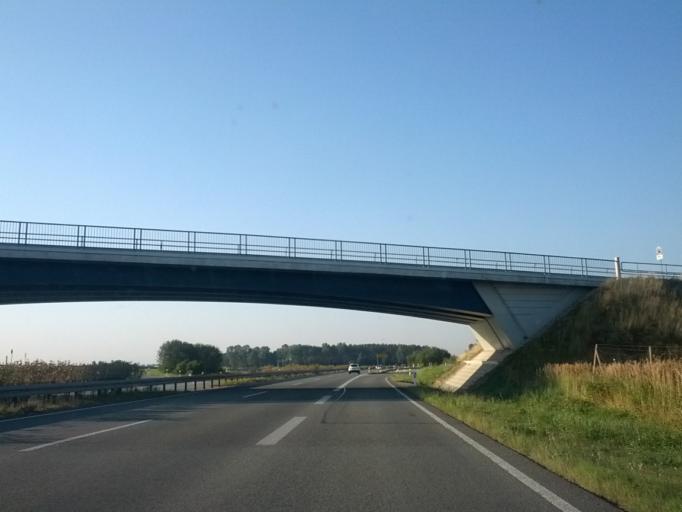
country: DE
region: Mecklenburg-Vorpommern
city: Brandshagen
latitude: 54.1679
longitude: 13.1762
